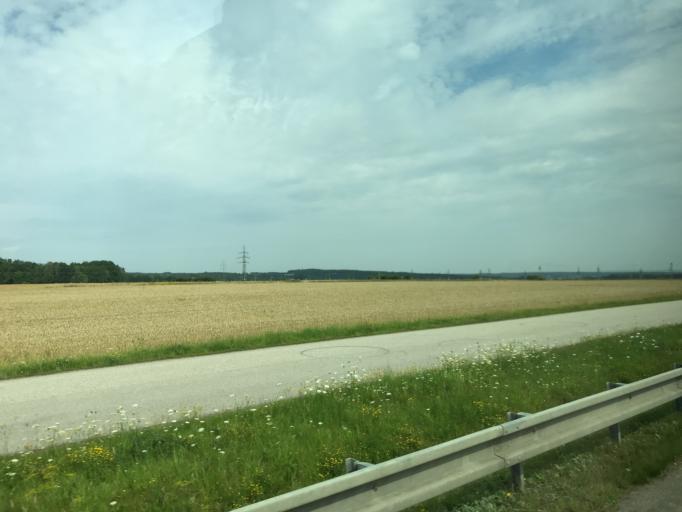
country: CZ
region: Jihocesky
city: Kamenny Ujezd
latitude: 48.8952
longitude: 14.4377
